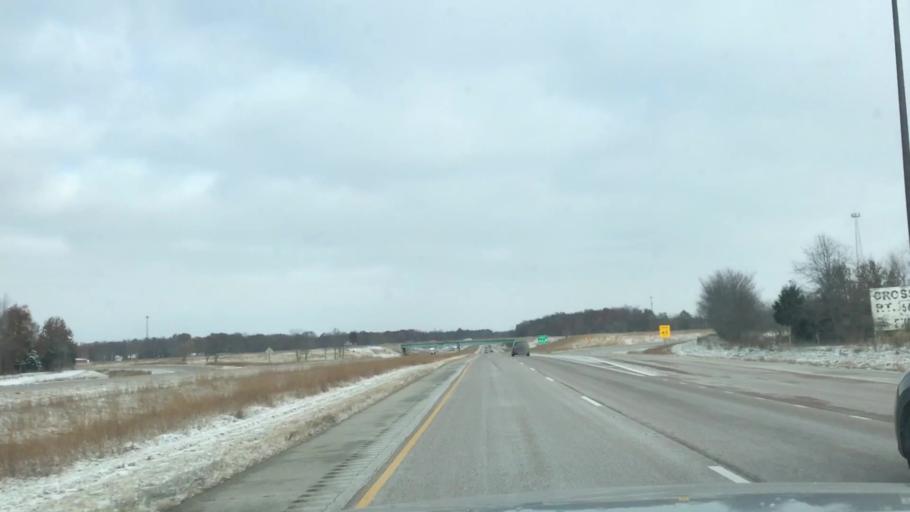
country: US
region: Illinois
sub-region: Macoupin County
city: Mount Olive
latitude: 39.0679
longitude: -89.7556
